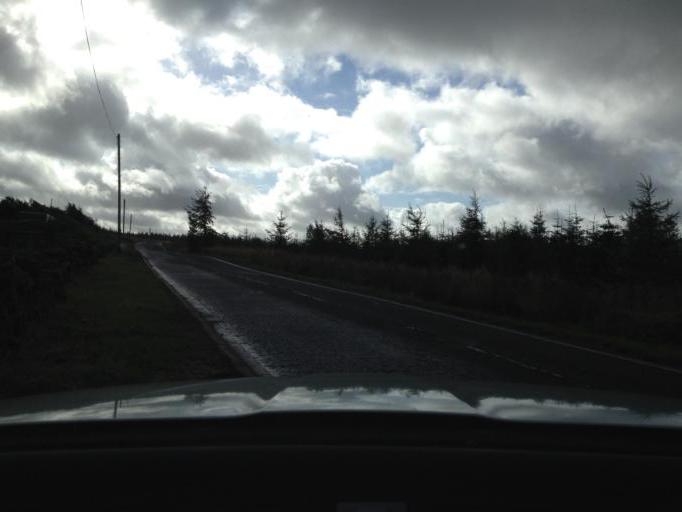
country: GB
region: Scotland
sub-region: West Lothian
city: West Calder
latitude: 55.8197
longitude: -3.5235
